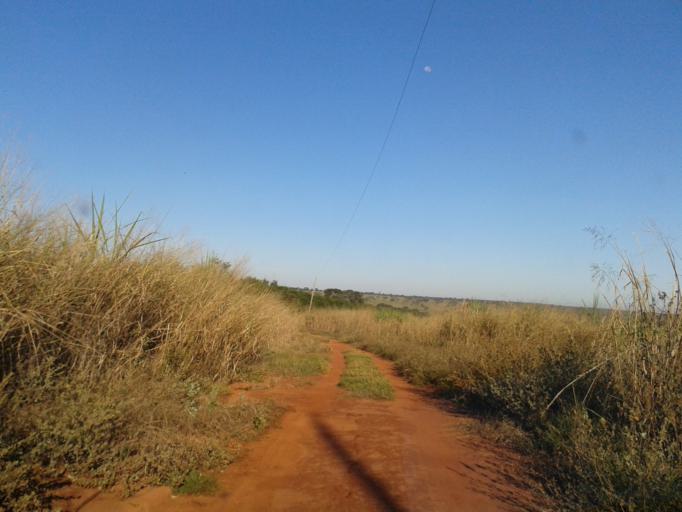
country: BR
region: Minas Gerais
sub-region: Santa Vitoria
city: Santa Vitoria
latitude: -19.0229
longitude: -50.3653
